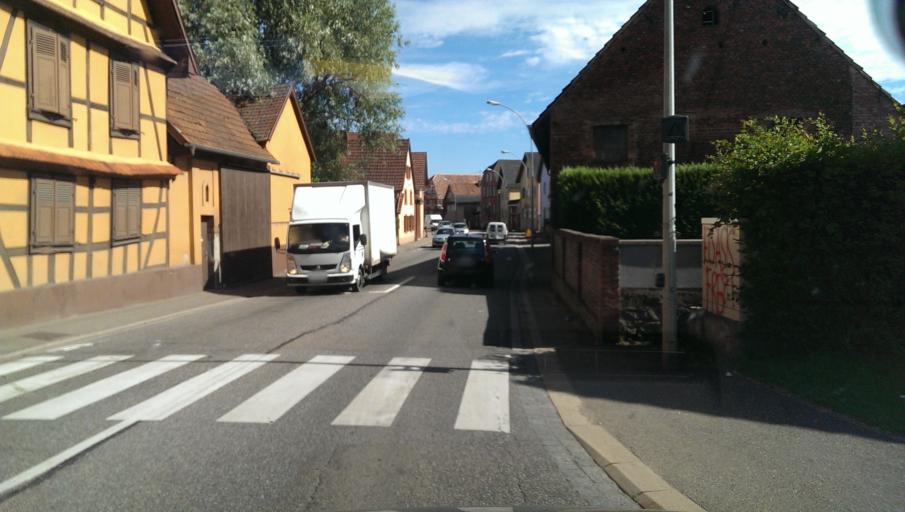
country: FR
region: Alsace
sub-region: Departement du Bas-Rhin
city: Mommenheim
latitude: 48.7585
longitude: 7.6393
